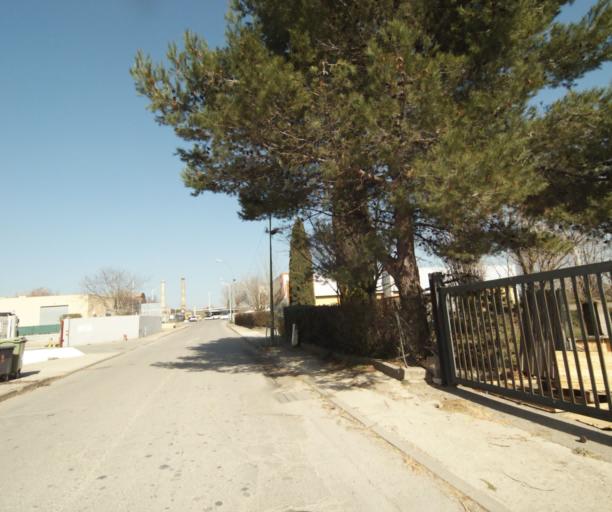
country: FR
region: Provence-Alpes-Cote d'Azur
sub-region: Departement des Bouches-du-Rhone
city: Gardanne
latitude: 43.4474
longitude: 5.4553
